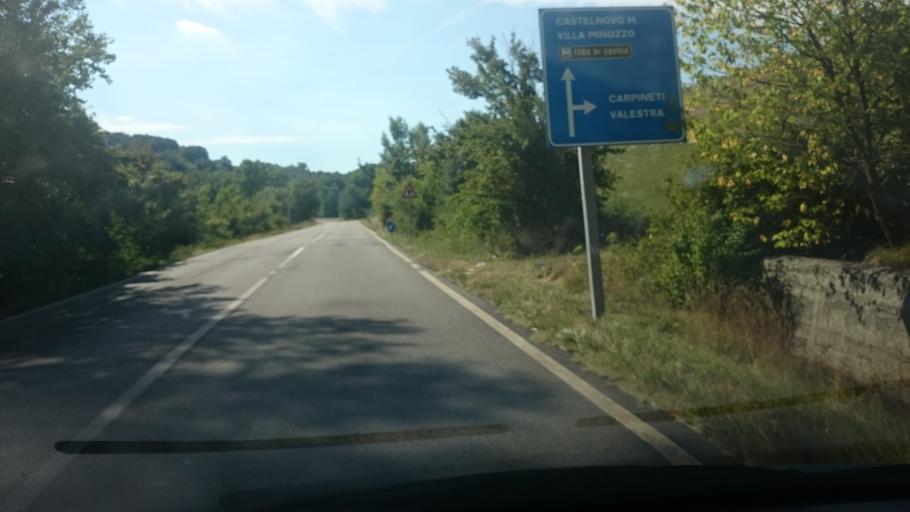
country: IT
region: Emilia-Romagna
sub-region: Provincia di Reggio Emilia
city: Toano
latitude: 44.4125
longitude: 10.5895
